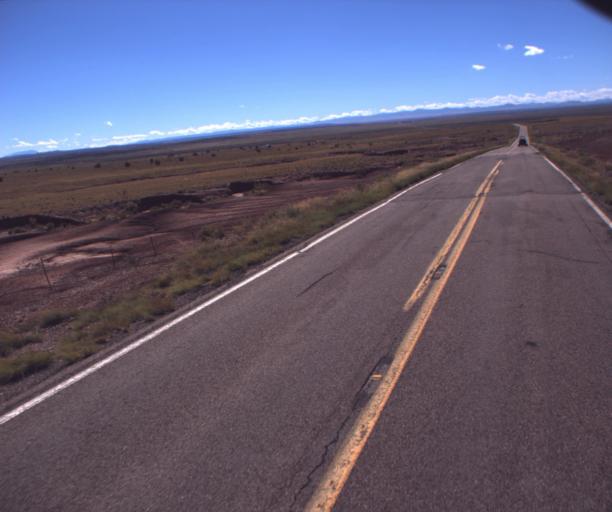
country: US
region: Arizona
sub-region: Apache County
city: Saint Johns
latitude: 34.6464
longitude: -109.3021
